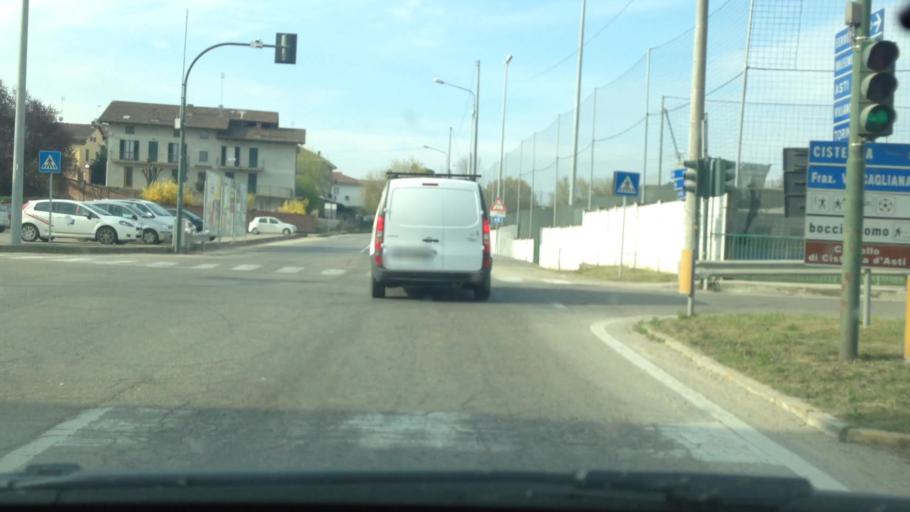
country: IT
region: Piedmont
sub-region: Provincia di Asti
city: San Damiano d'Asti
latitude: 44.8347
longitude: 8.0622
